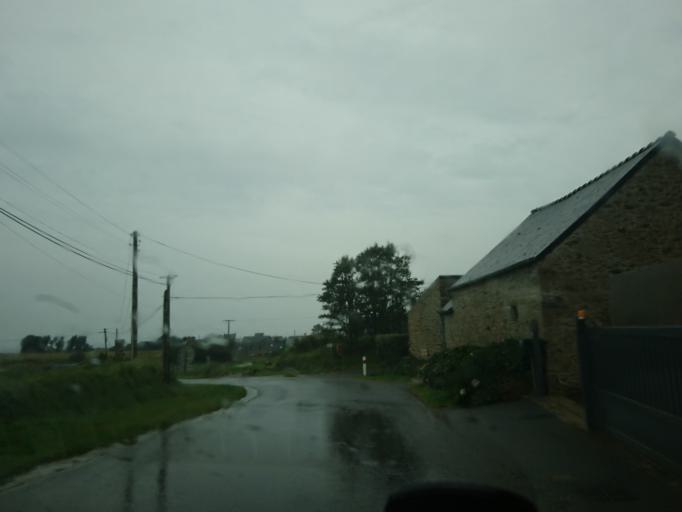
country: FR
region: Brittany
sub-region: Departement du Finistere
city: Plouguerneau
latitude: 48.6195
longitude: -4.4599
